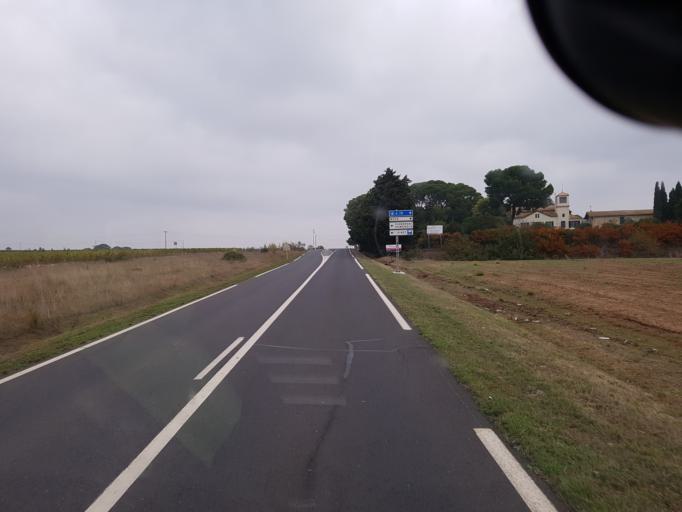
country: FR
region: Languedoc-Roussillon
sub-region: Departement de l'Herault
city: Pinet
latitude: 43.3880
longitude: 3.5371
